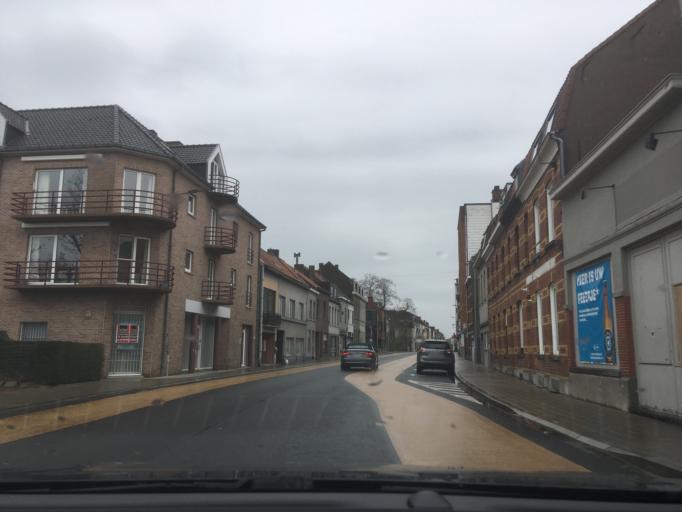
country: BE
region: Flanders
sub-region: Provincie West-Vlaanderen
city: Kortrijk
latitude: 50.8173
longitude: 3.2698
